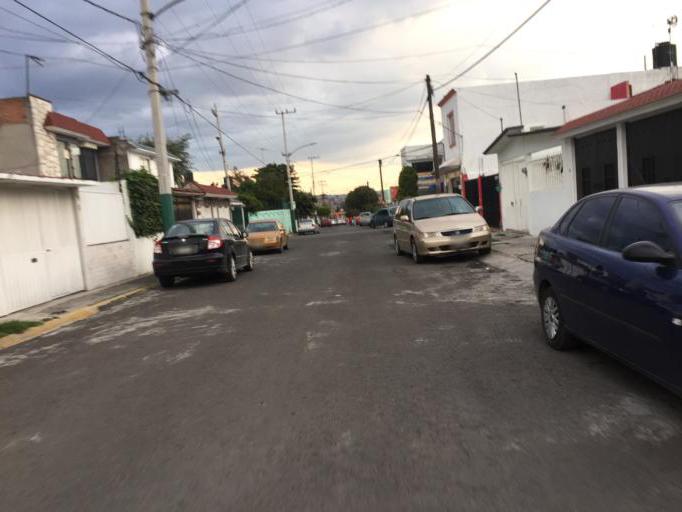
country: MX
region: Mexico
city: Cuautitlan Izcalli
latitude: 19.6517
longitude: -99.2103
